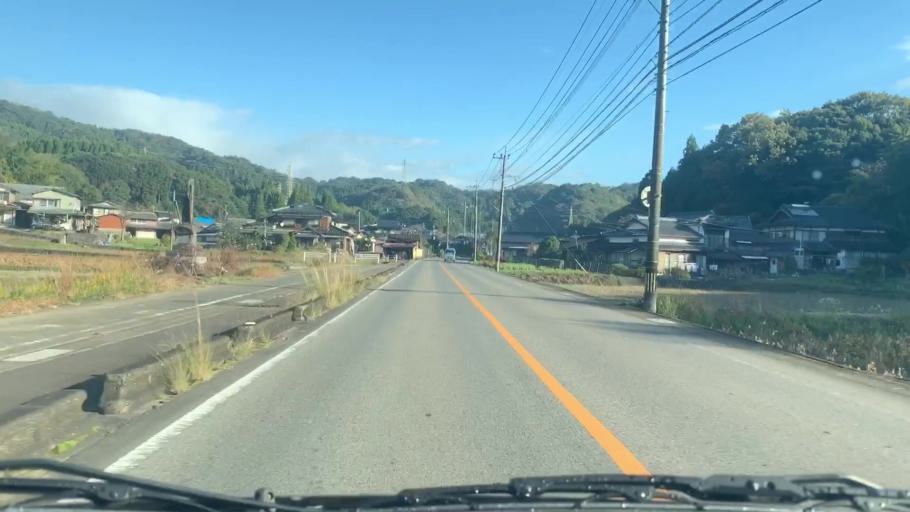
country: JP
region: Saga Prefecture
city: Takeocho-takeo
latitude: 33.2303
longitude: 130.0601
